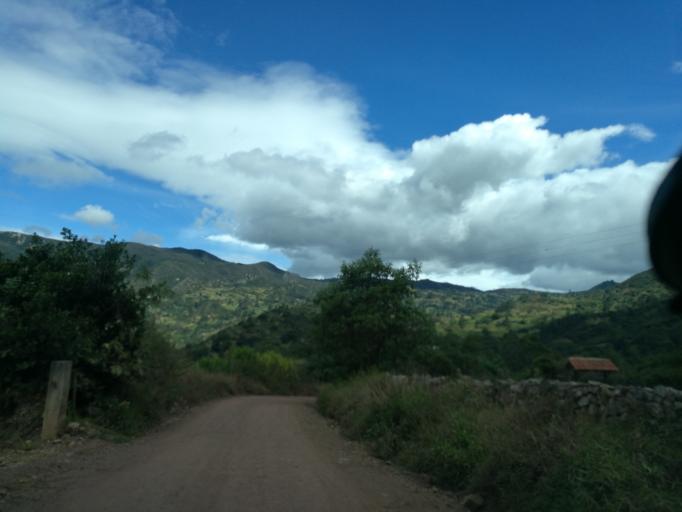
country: CO
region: Boyaca
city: Socota
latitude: 6.1185
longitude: -72.7145
